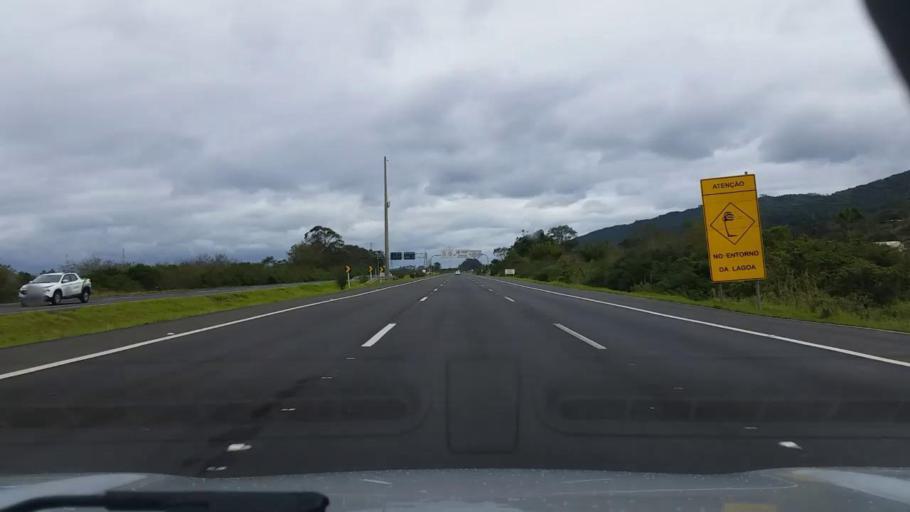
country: BR
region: Rio Grande do Sul
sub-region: Osorio
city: Osorio
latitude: -29.8979
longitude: -50.3029
